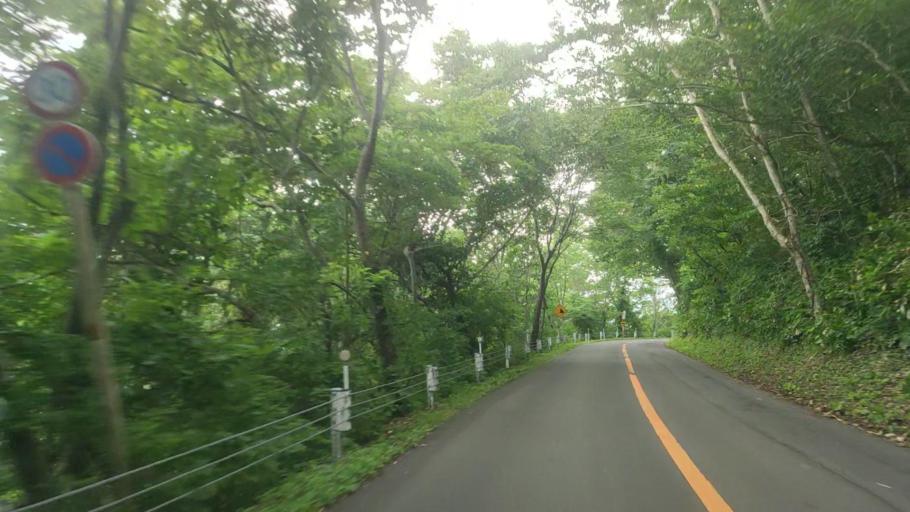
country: JP
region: Hokkaido
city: Hakodate
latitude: 41.7624
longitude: 140.7072
